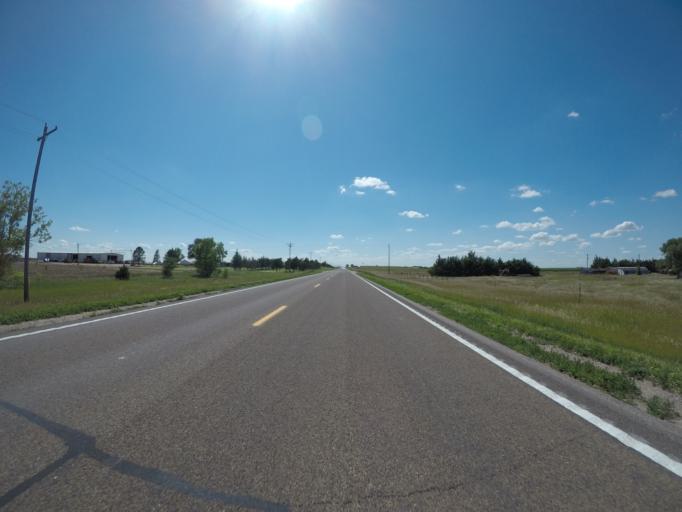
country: US
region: Nebraska
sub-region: Chase County
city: Imperial
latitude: 40.5375
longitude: -101.8361
